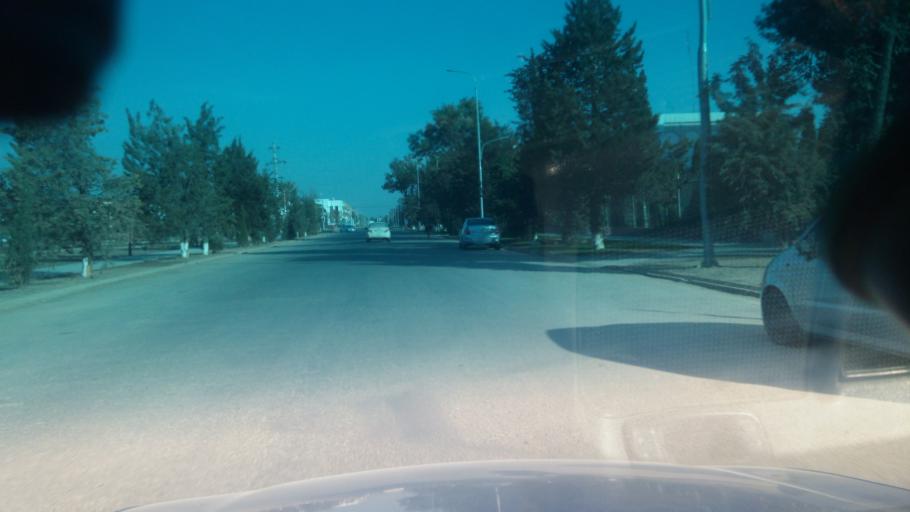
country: UZ
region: Sirdaryo
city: Guliston
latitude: 40.4974
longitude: 68.7767
